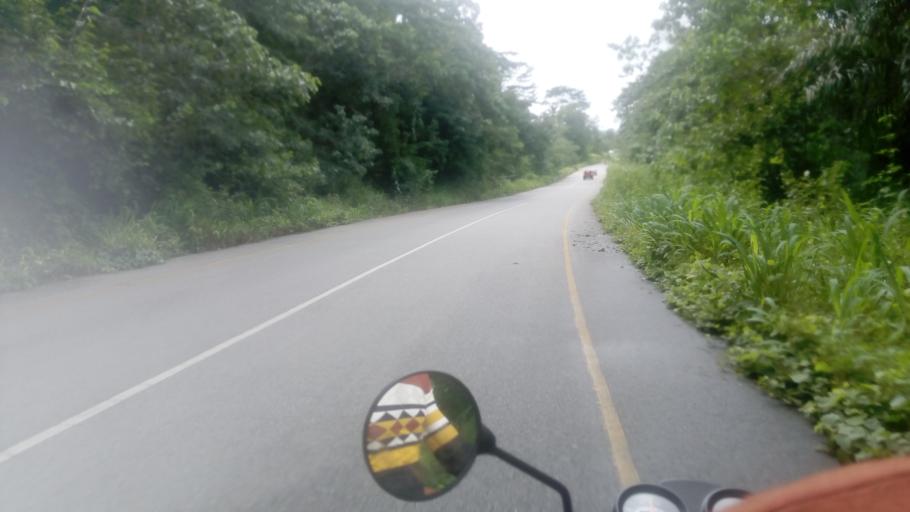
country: SL
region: Northern Province
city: Makali
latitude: 8.6343
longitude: -11.6719
